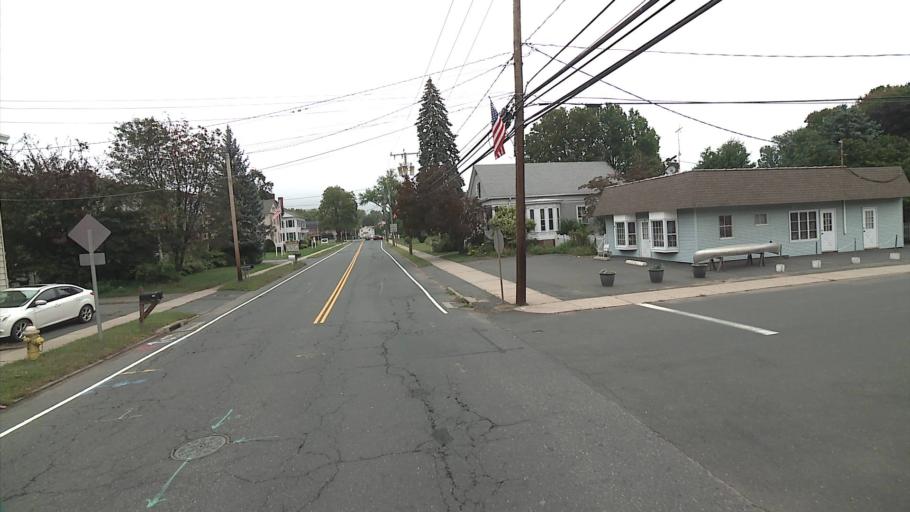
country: US
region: Connecticut
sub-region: Hartford County
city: Windsor Locks
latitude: 41.9274
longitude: -72.6180
